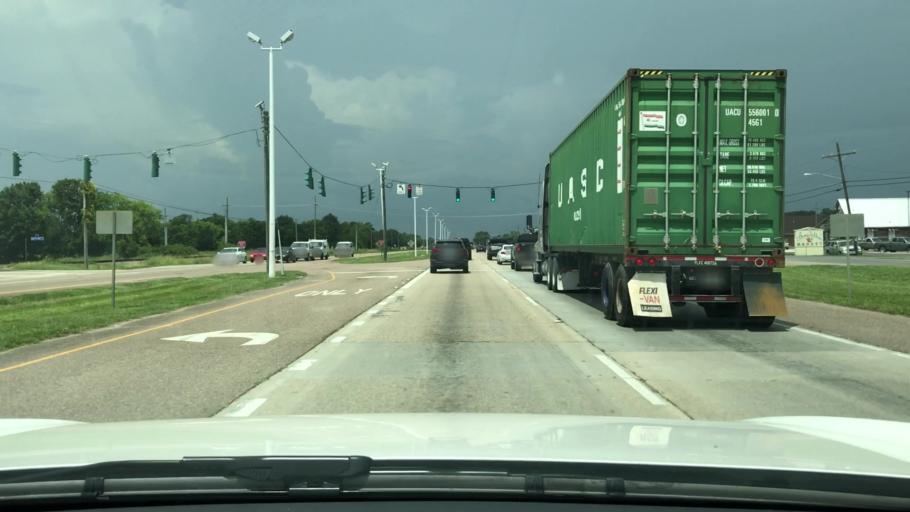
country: US
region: Louisiana
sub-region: West Baton Rouge Parish
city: Brusly
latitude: 30.3734
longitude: -91.2546
